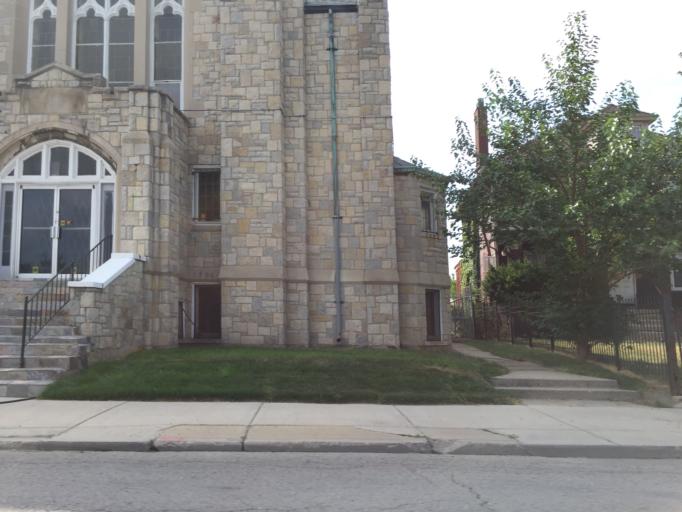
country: US
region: Michigan
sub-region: Wayne County
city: Grosse Pointe Park
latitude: 42.3640
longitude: -82.9768
